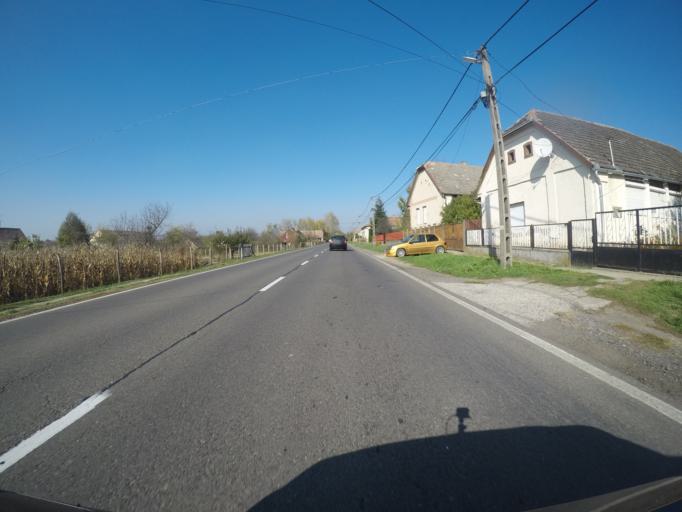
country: HU
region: Tolna
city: Szedres
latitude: 46.5108
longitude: 18.6655
